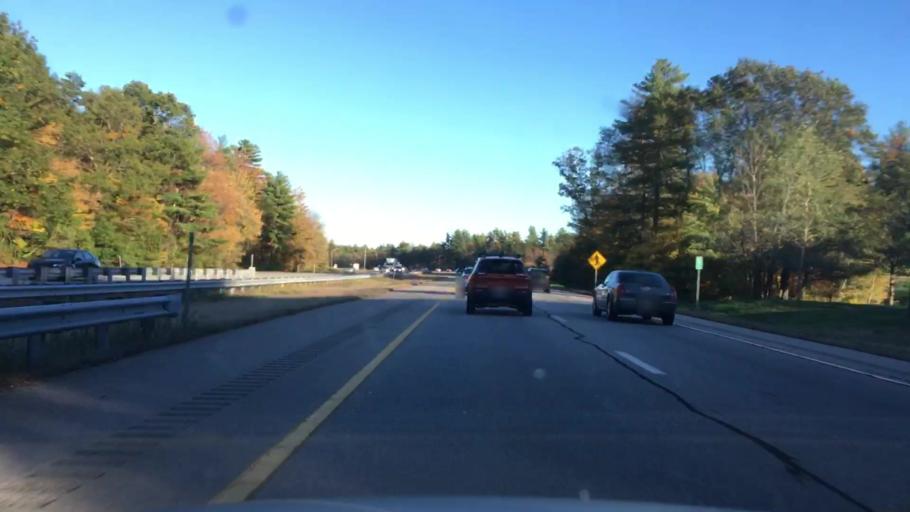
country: US
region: New Hampshire
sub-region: Rockingham County
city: Epping
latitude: 43.0267
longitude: -71.1165
